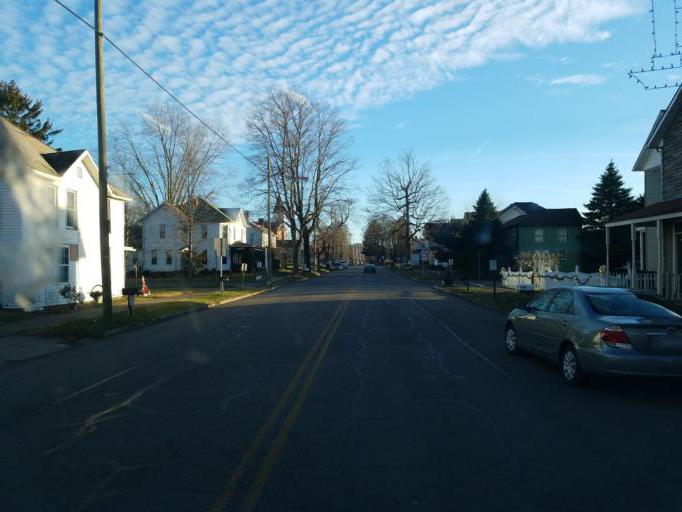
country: US
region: Ohio
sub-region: Muskingum County
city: Dresden
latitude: 40.1199
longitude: -82.0102
